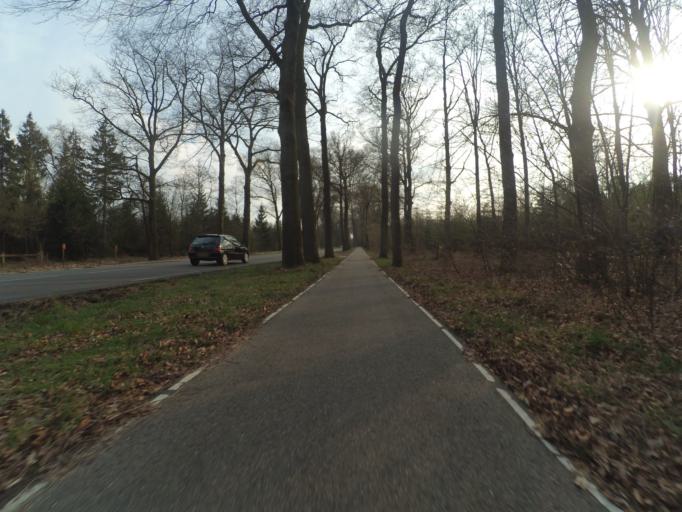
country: NL
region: Gelderland
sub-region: Gemeente Apeldoorn
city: Beekbergen
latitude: 52.1541
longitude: 5.8892
